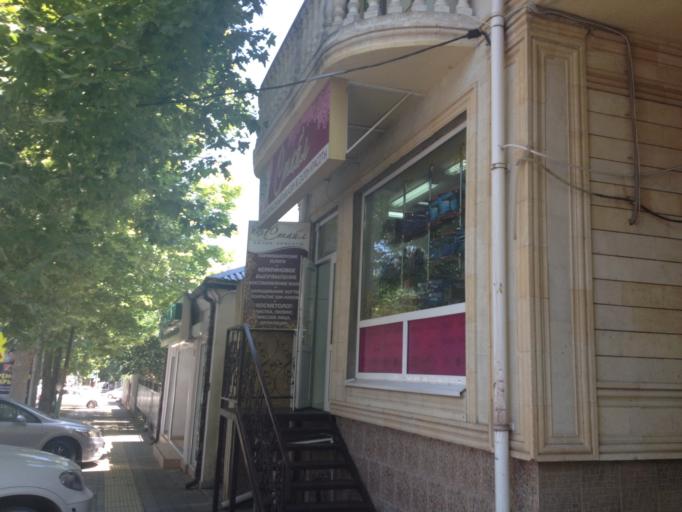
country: RU
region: Krasnodarskiy
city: Anapa
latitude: 44.8931
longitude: 37.3150
